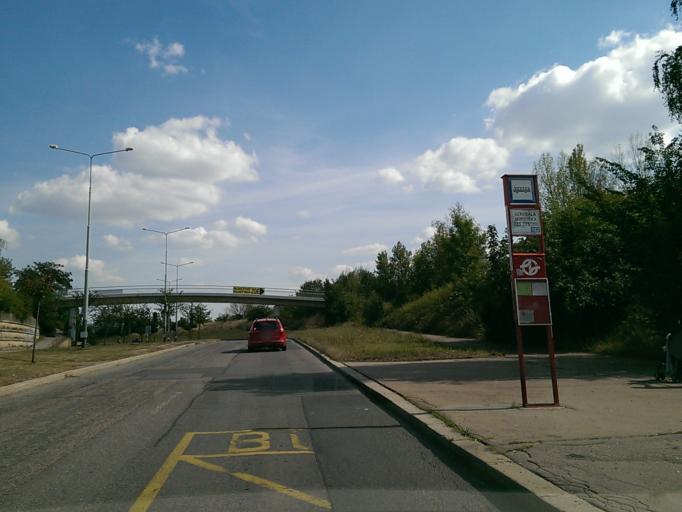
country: CZ
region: Praha
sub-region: Praha 14
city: Hostavice
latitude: 50.1026
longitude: 14.5638
